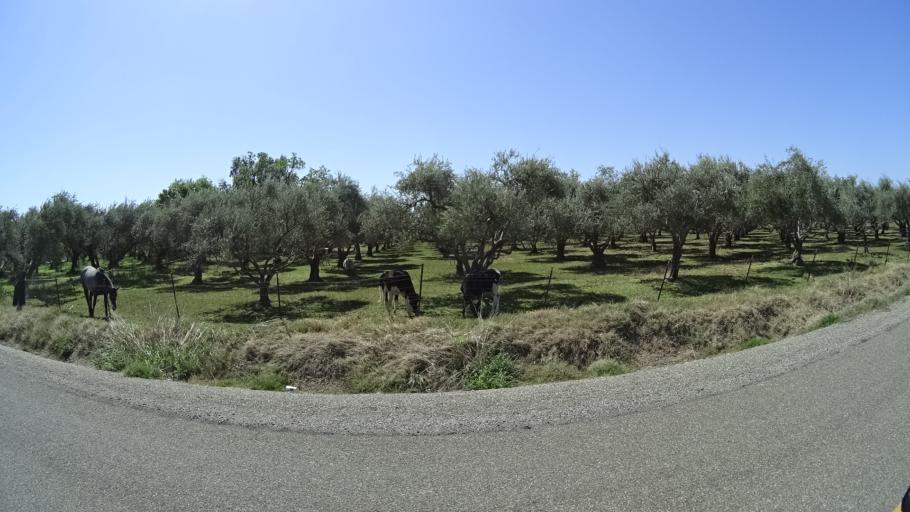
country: US
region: California
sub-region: Glenn County
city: Orland
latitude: 39.7871
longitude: -122.1791
